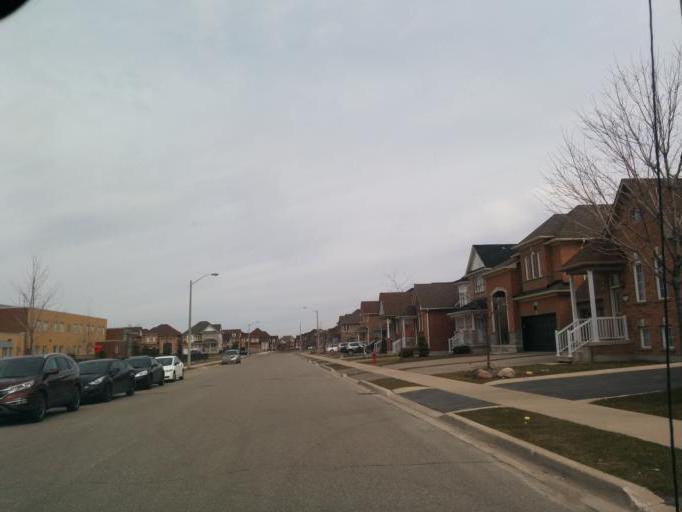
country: CA
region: Ontario
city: Brampton
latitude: 43.7196
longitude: -79.8260
